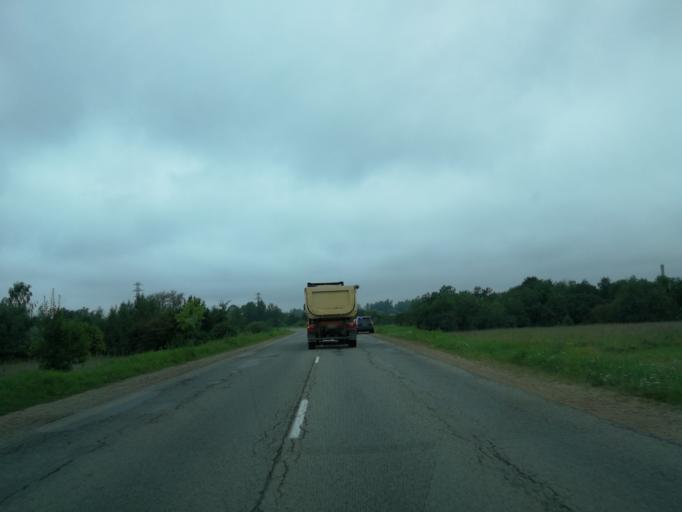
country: LV
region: Jekabpils Rajons
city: Jekabpils
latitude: 56.4995
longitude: 25.9008
